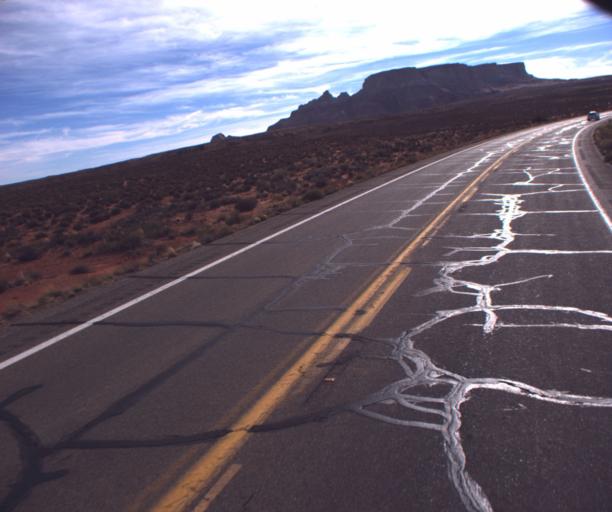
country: US
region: Arizona
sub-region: Coconino County
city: LeChee
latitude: 36.8792
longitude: -111.3458
